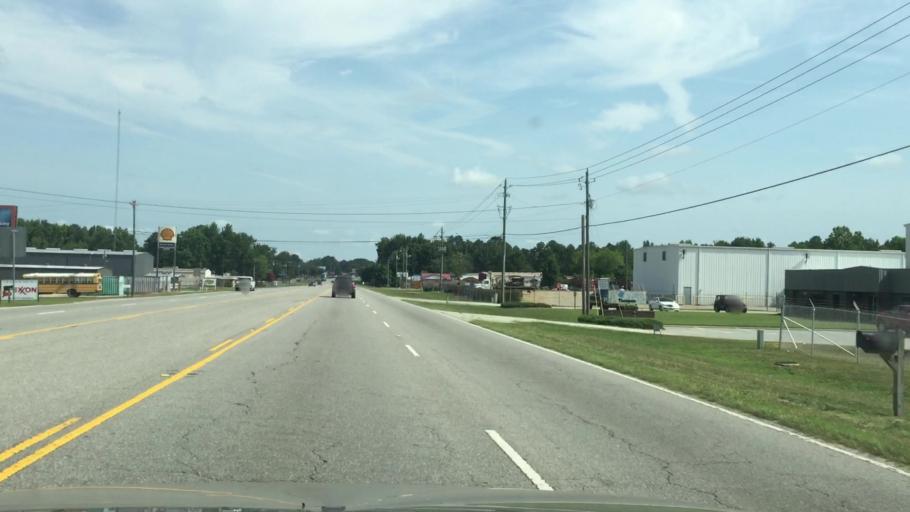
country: US
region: South Carolina
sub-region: Sumter County
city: South Sumter
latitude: 33.8939
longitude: -80.3520
